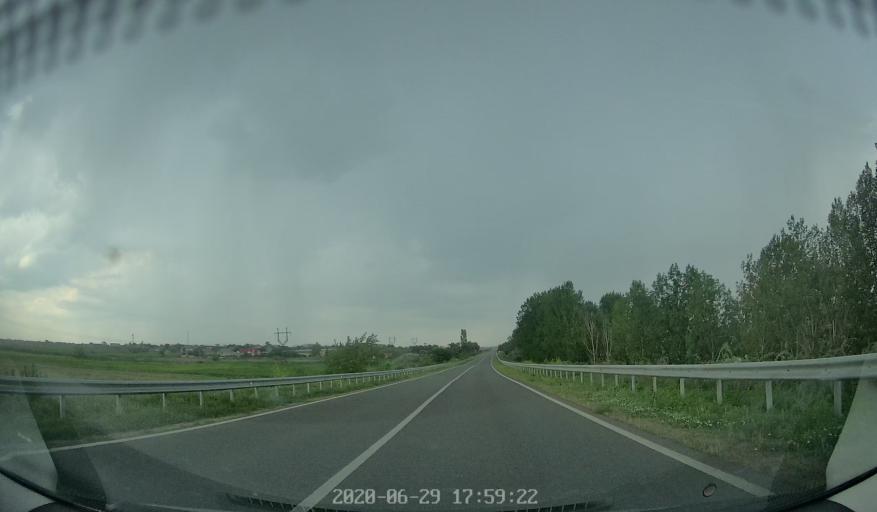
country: UA
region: Odessa
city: Starokozache
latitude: 46.3948
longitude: 30.0902
